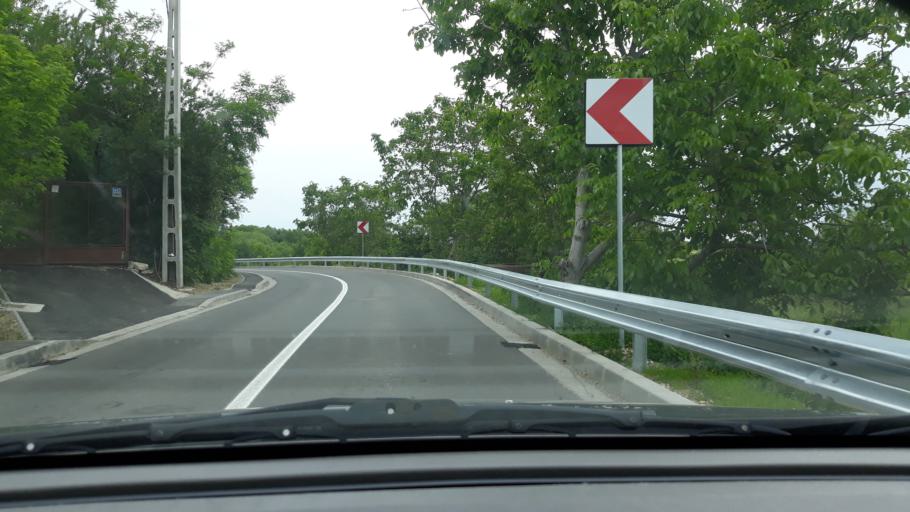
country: RO
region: Bihor
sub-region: Comuna Osorheiu
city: Osorheiu
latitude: 47.0608
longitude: 22.0267
